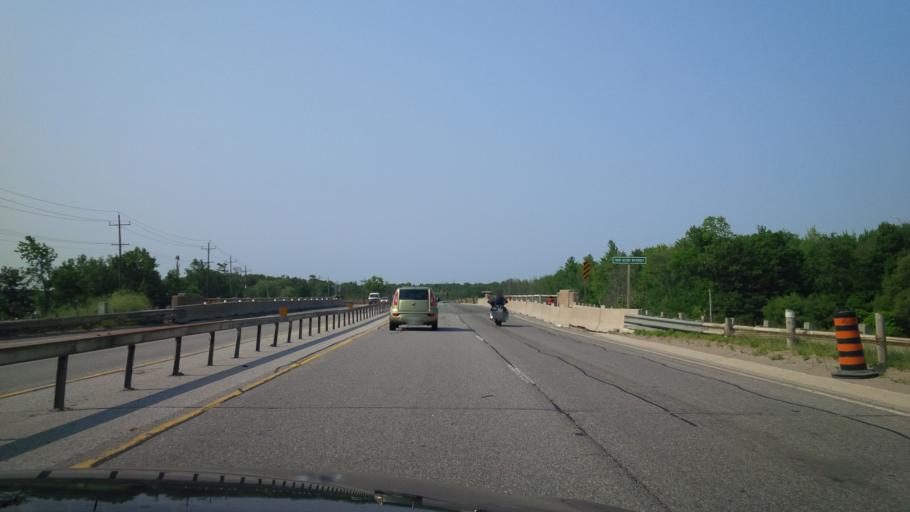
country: CA
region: Ontario
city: Orillia
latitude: 44.7490
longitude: -79.3420
